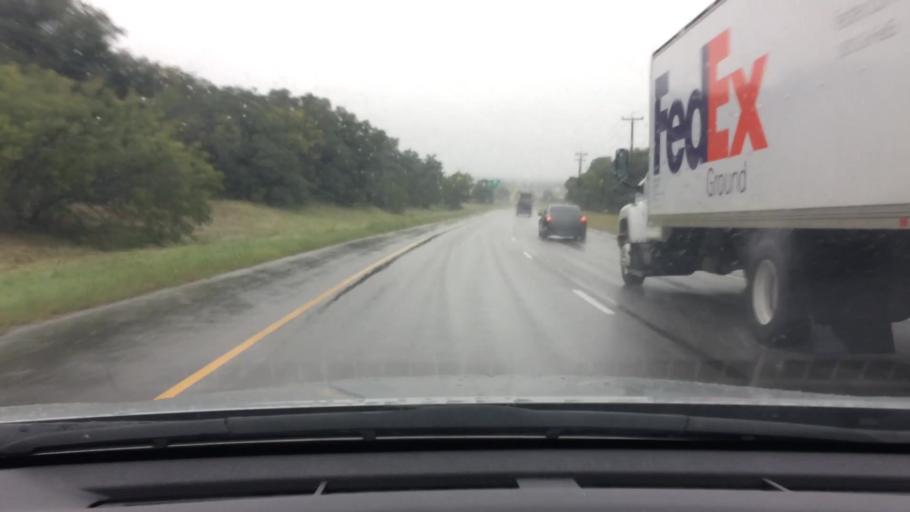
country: US
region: Texas
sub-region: Bexar County
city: Leon Valley
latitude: 29.4848
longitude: -98.7080
